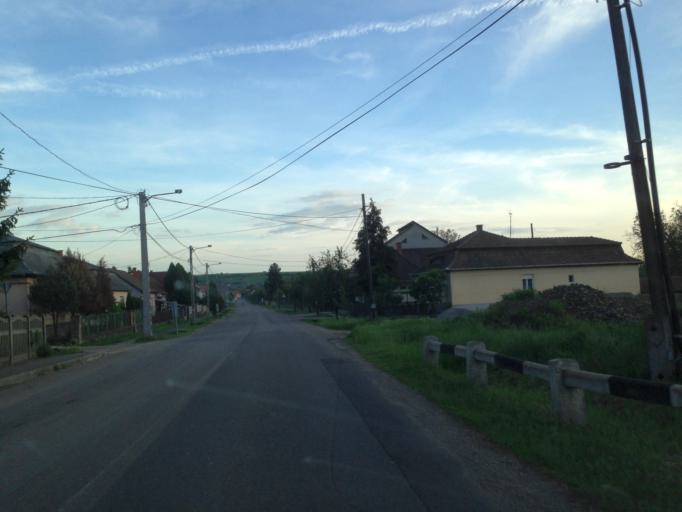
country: HU
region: Nograd
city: Tar
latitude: 47.9562
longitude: 19.7467
